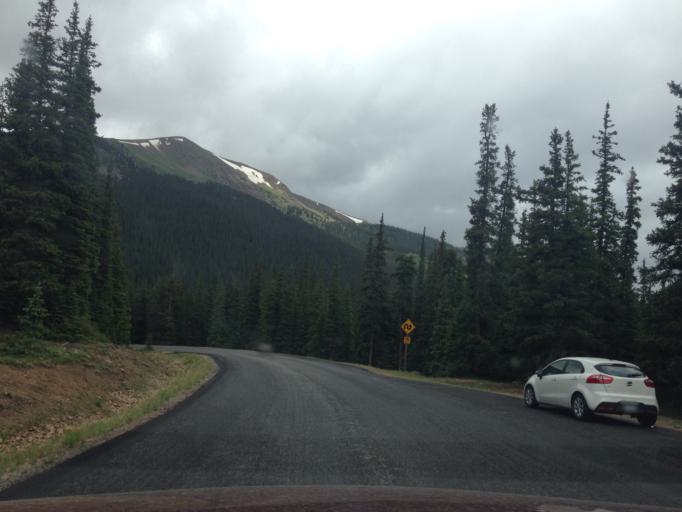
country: US
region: Colorado
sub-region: Clear Creek County
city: Georgetown
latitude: 39.6076
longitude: -105.7139
